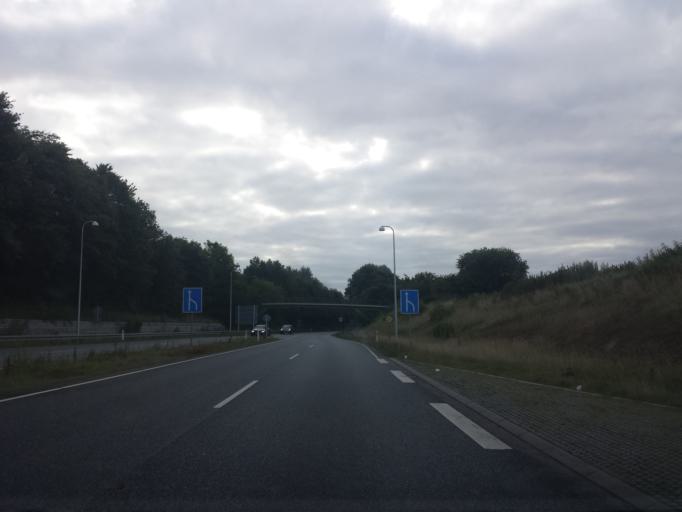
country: DK
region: South Denmark
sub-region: Sonderborg Kommune
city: Sonderborg
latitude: 54.9327
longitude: 9.8102
